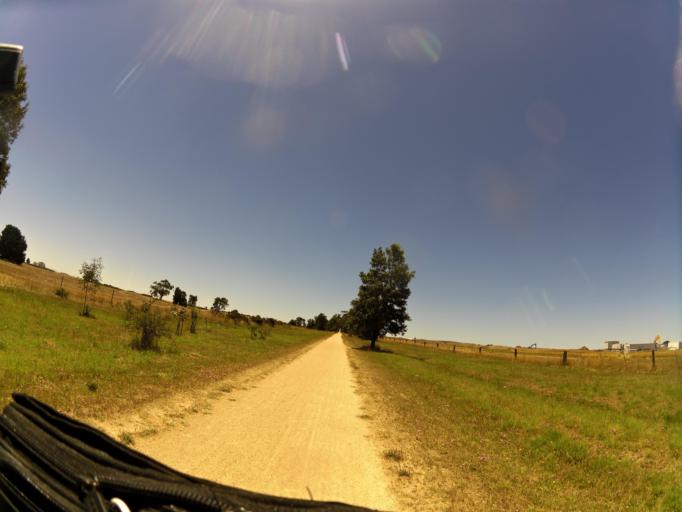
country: AU
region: Victoria
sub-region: Ballarat North
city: Newington
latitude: -37.5481
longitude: 143.7600
